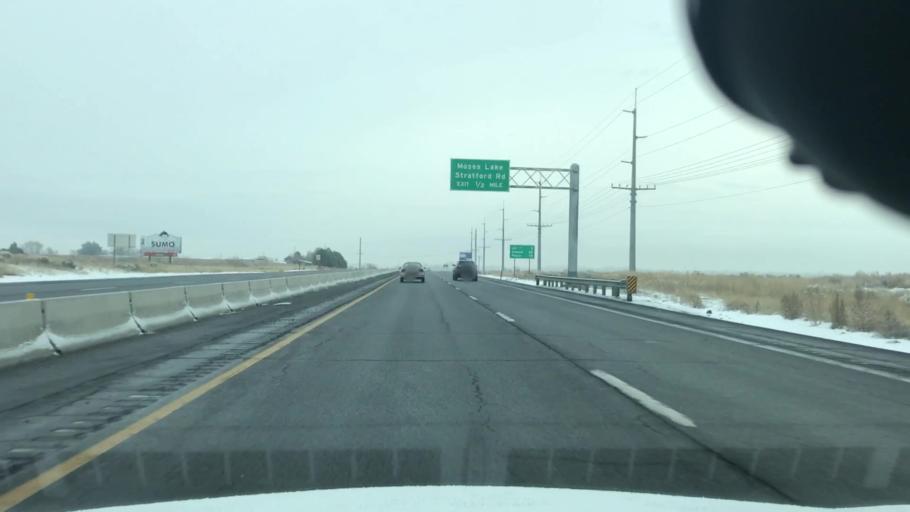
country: US
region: Washington
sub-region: Grant County
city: Moses Lake
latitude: 47.1483
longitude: -119.2911
